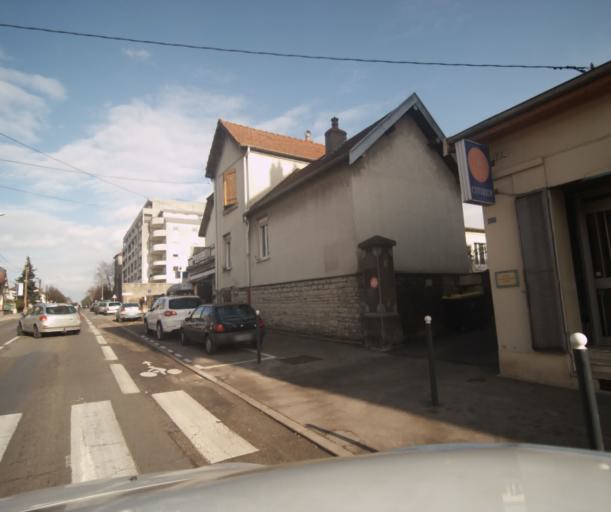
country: FR
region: Franche-Comte
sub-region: Departement du Doubs
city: Besancon
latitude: 47.2551
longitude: 6.0399
